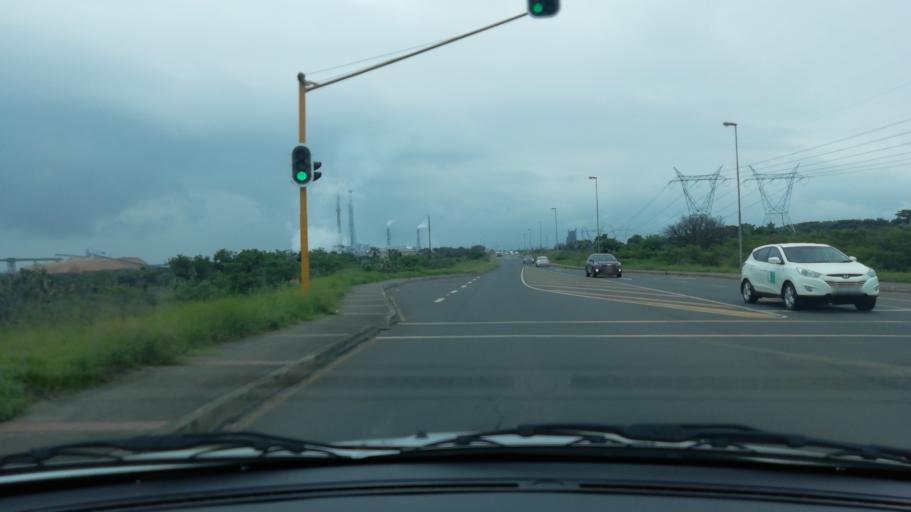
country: ZA
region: KwaZulu-Natal
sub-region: uThungulu District Municipality
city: Richards Bay
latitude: -28.7645
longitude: 32.0379
